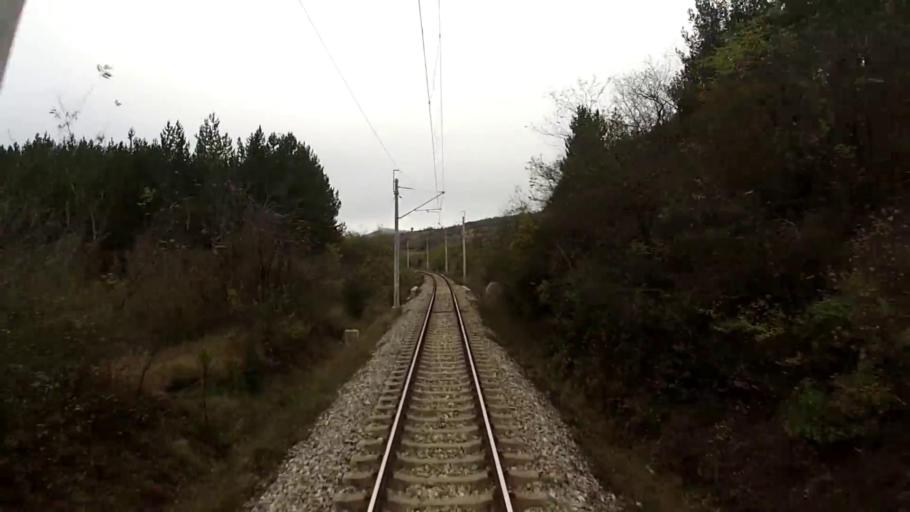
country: BG
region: Sofiya
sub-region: Obshtina Dragoman
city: Dragoman
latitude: 42.9425
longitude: 22.9014
